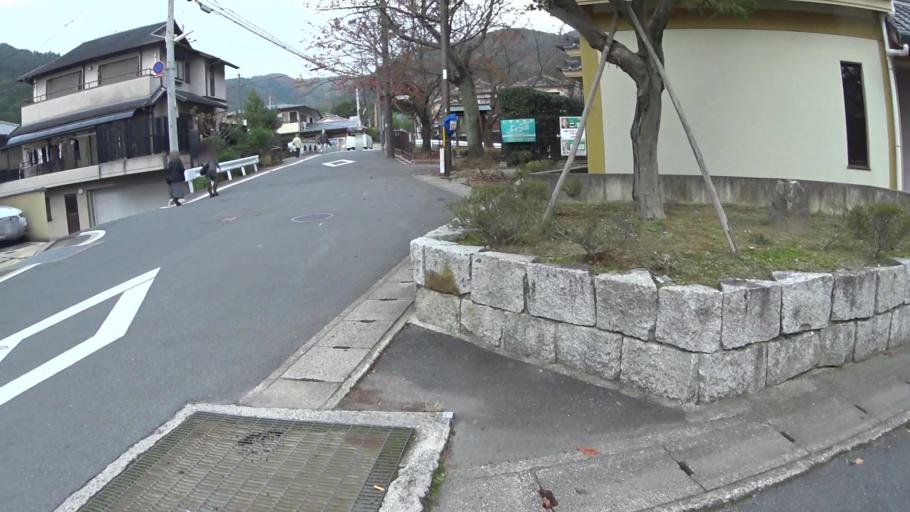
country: JP
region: Shiga Prefecture
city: Otsu-shi
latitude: 34.9967
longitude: 135.8194
